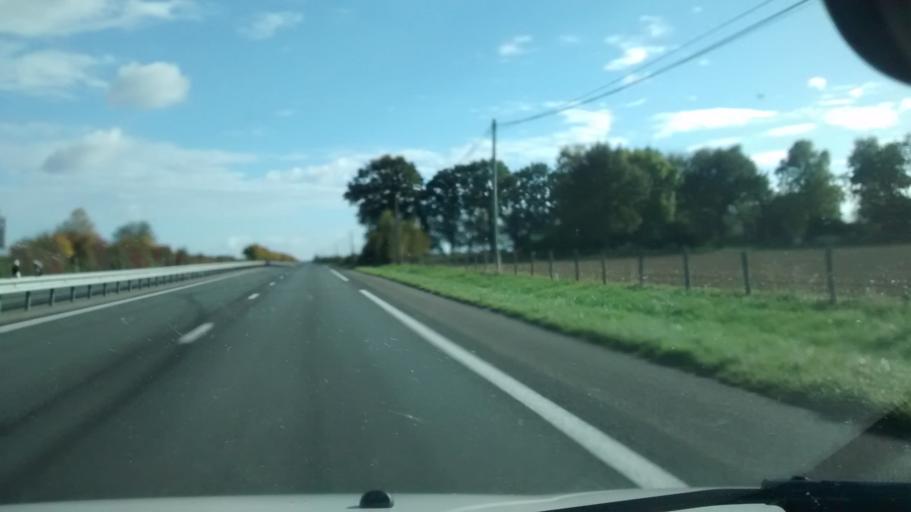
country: FR
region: Pays de la Loire
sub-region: Departement de Maine-et-Loire
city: Pouance
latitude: 47.7349
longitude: -1.1396
